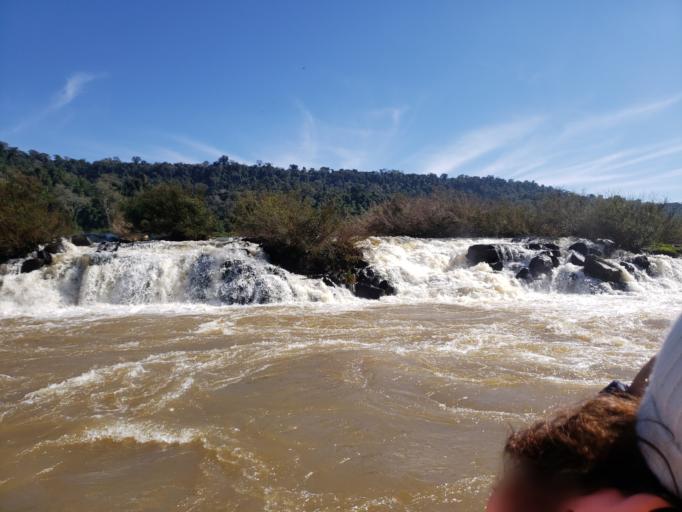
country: BR
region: Rio Grande do Sul
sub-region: Tres Passos
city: Tres Passos
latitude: -27.1512
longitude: -53.8877
